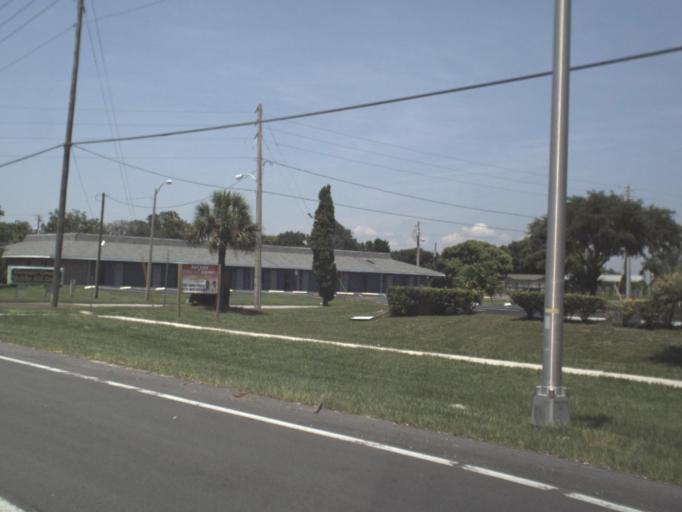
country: US
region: Florida
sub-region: Pasco County
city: Bayonet Point
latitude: 28.3133
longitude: -82.6992
